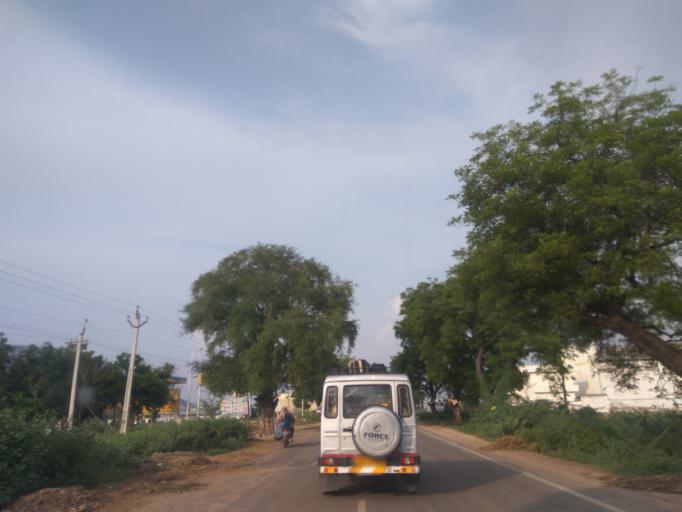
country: IN
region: Andhra Pradesh
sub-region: Guntur
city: Vinukonda
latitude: 16.0367
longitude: 79.7262
